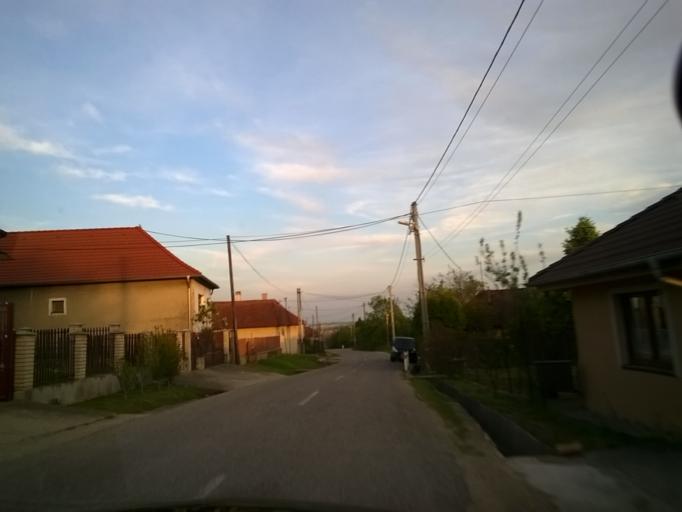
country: SK
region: Nitriansky
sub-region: Okres Nitra
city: Nitra
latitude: 48.3791
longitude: 18.1749
